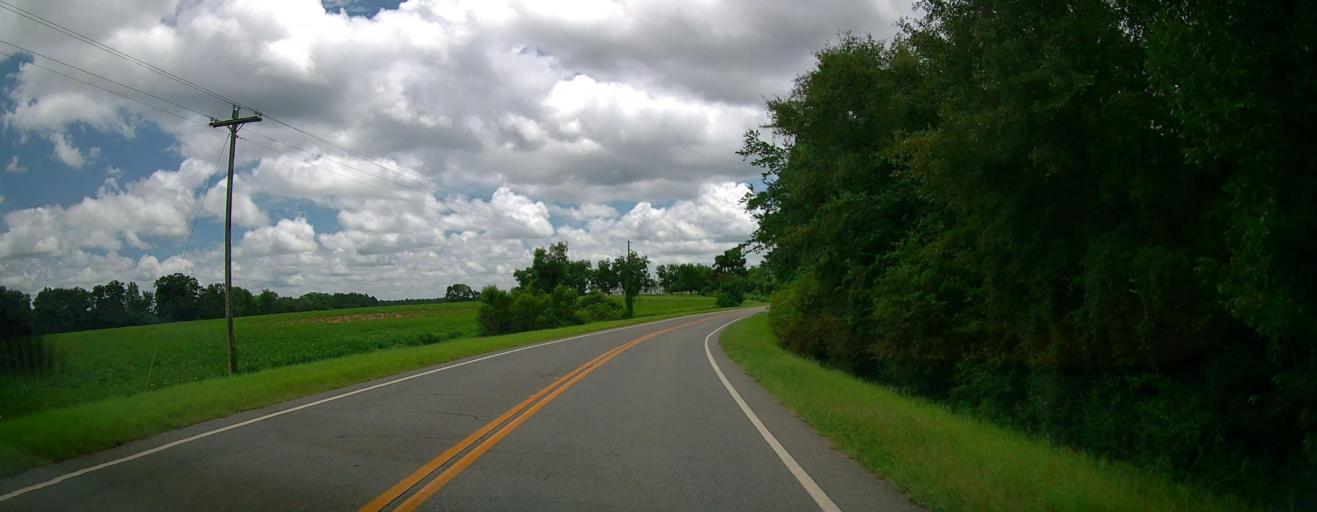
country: US
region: Georgia
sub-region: Wilcox County
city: Rochelle
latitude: 31.9913
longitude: -83.5466
